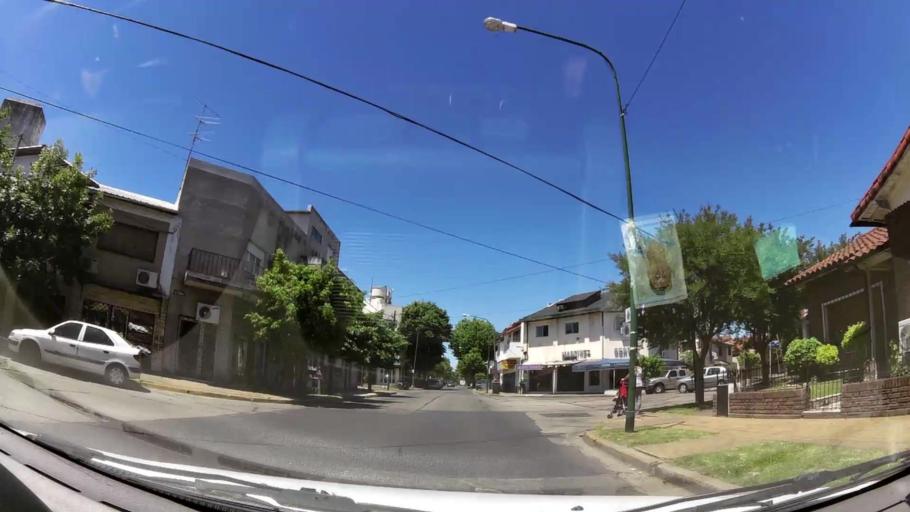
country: AR
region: Buenos Aires
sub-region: Partido de San Isidro
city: San Isidro
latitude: -34.4909
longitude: -58.5166
